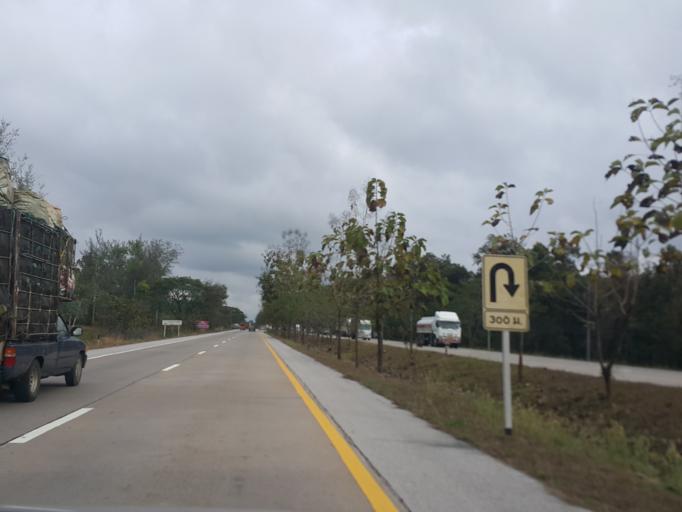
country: TH
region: Lampang
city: Hang Chat
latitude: 18.3230
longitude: 99.2967
